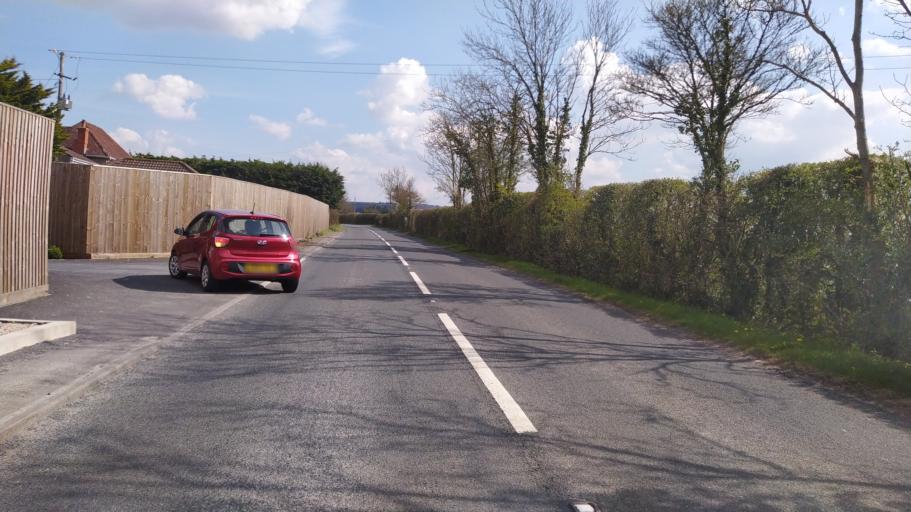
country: GB
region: England
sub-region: Wiltshire
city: Corsley
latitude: 51.2167
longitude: -2.2812
